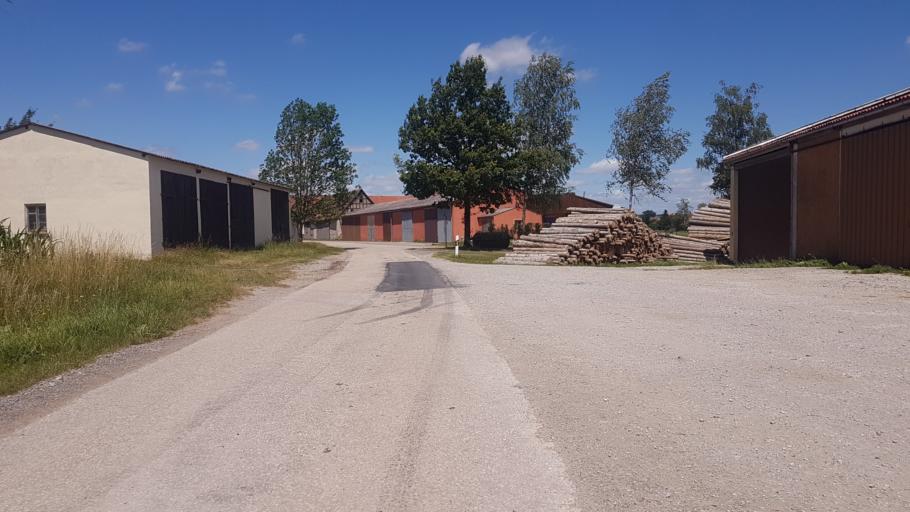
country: DE
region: Bavaria
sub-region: Regierungsbezirk Mittelfranken
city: Leutershausen
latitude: 49.2915
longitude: 10.4095
